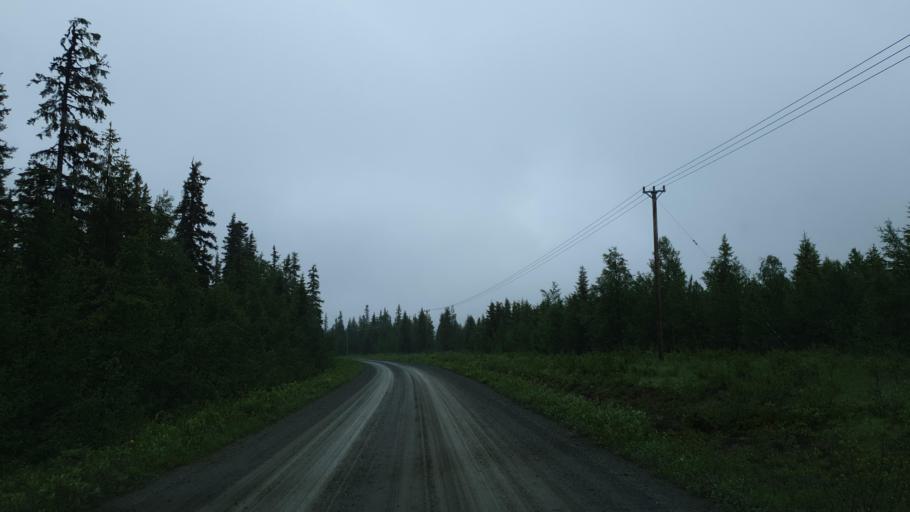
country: SE
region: Vaesterbotten
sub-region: Vilhelmina Kommun
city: Sjoberg
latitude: 65.3117
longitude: 15.9685
